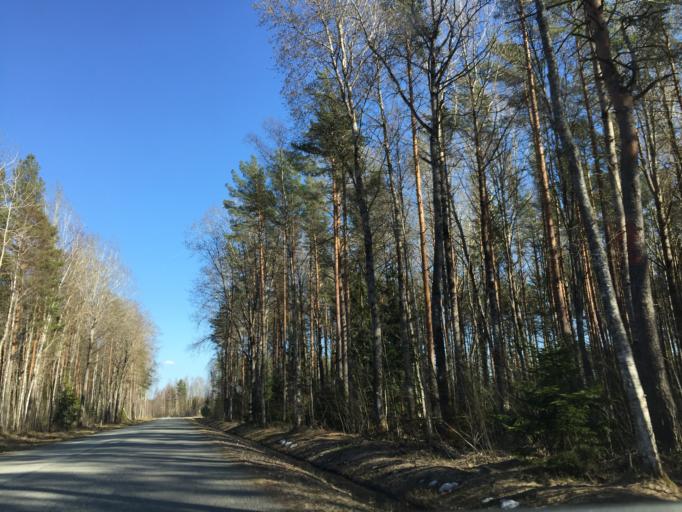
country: EE
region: Ida-Virumaa
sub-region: Johvi vald
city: Johvi
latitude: 59.0133
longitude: 27.5304
